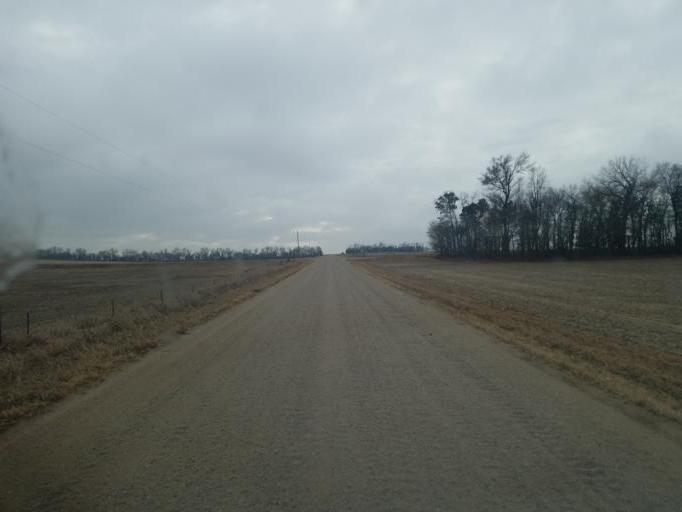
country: US
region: Nebraska
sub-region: Pierce County
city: Plainview
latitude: 42.4536
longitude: -97.7984
